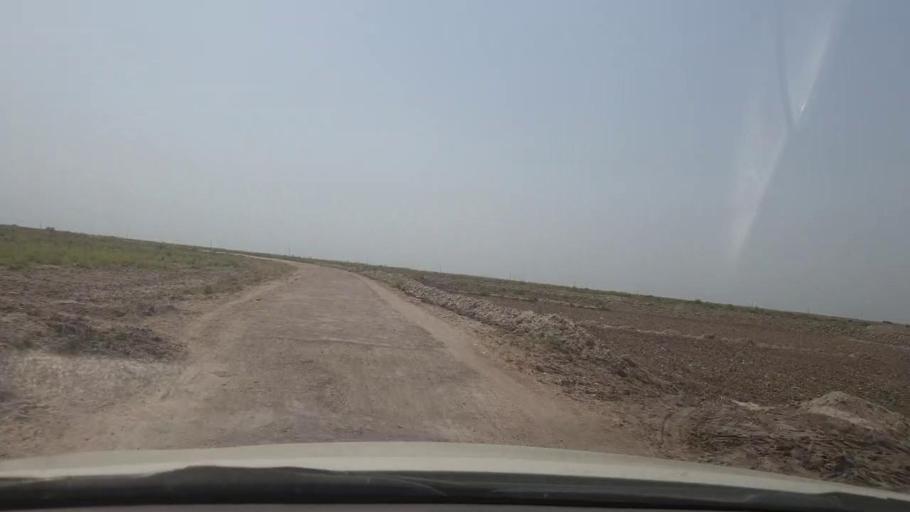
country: PK
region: Sindh
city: Garhi Yasin
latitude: 27.9889
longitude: 68.5099
